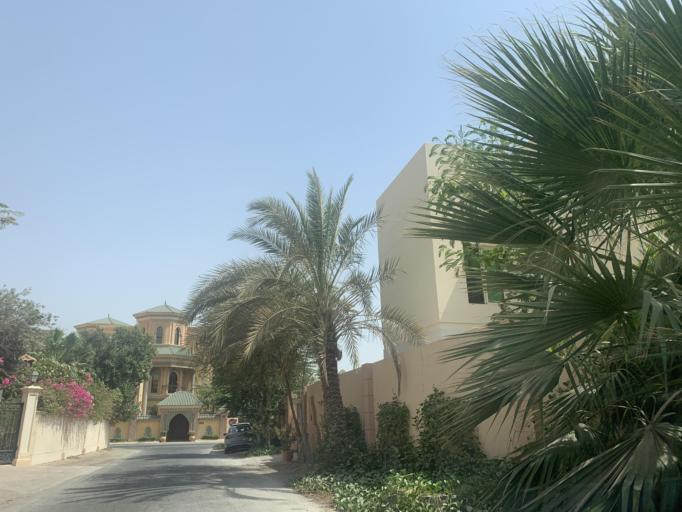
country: BH
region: Northern
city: Madinat `Isa
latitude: 26.1950
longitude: 50.4945
